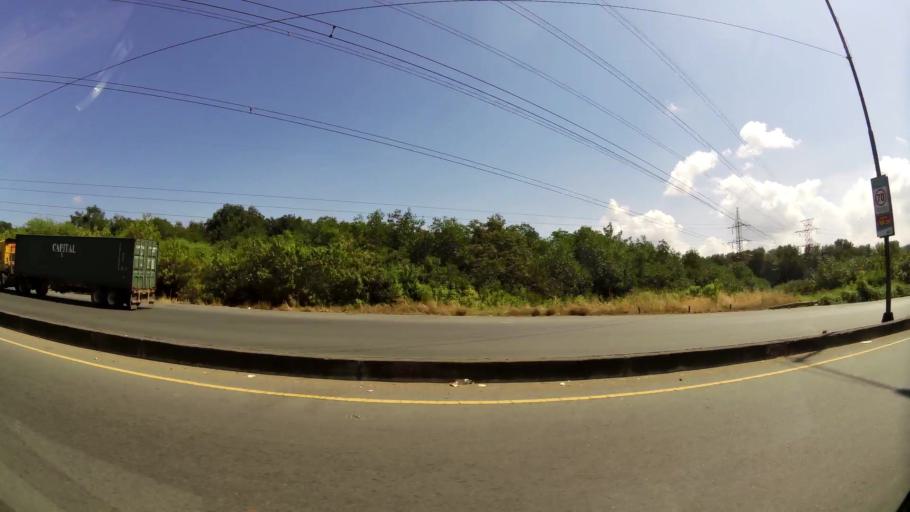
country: EC
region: Guayas
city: Santa Lucia
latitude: -2.1950
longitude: -79.9586
